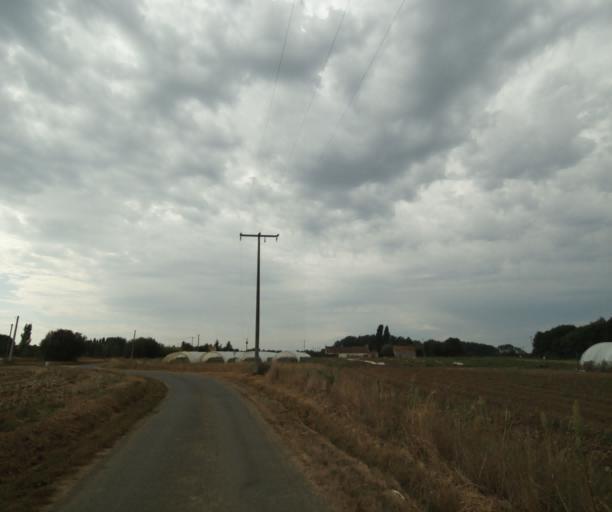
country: FR
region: Poitou-Charentes
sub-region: Departement de la Charente-Maritime
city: Tonnay-Charente
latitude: 45.9637
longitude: -0.8774
